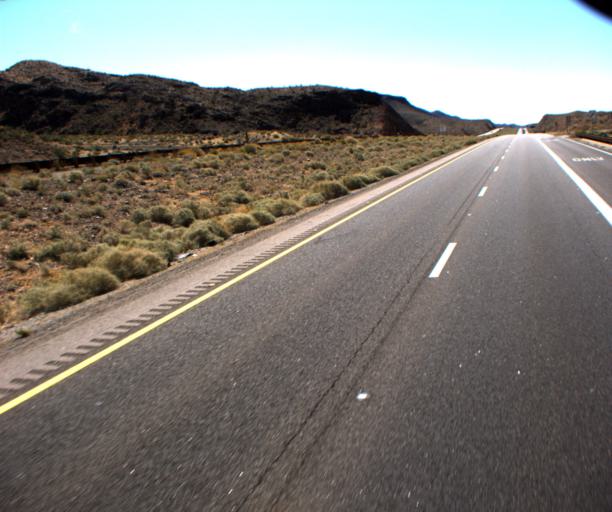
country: US
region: Nevada
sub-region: Clark County
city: Boulder City
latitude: 35.8841
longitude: -114.6181
